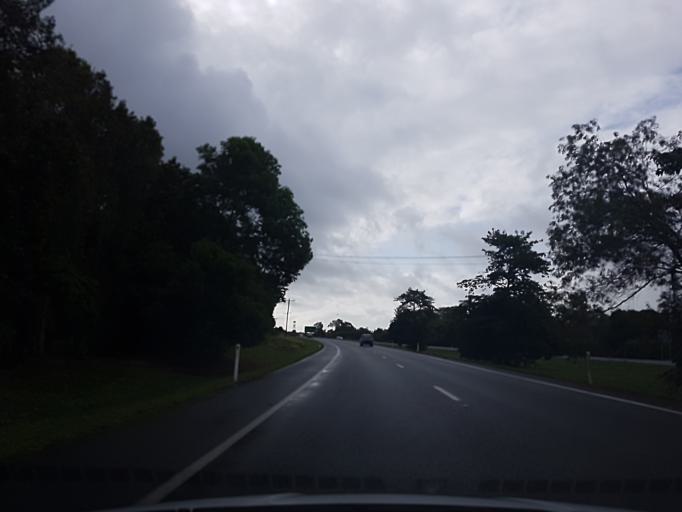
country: AU
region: Queensland
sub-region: Cairns
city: Trinity Beach
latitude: -16.8090
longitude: 145.6922
